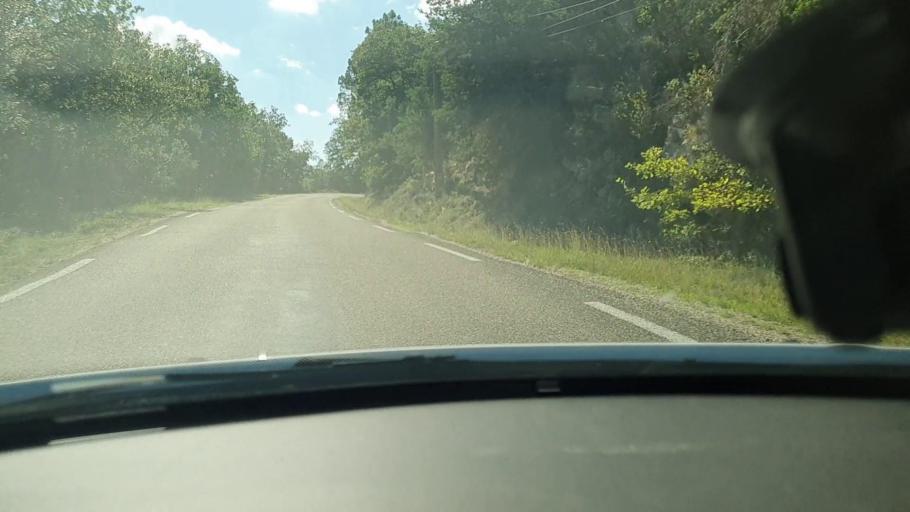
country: FR
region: Languedoc-Roussillon
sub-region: Departement du Gard
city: Goudargues
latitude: 44.1708
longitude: 4.4879
